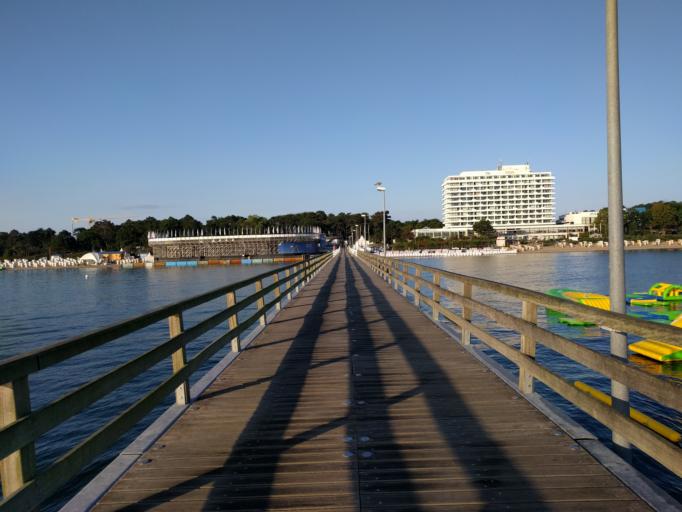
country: DE
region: Schleswig-Holstein
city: Timmendorfer Strand
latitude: 54.0018
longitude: 10.7846
